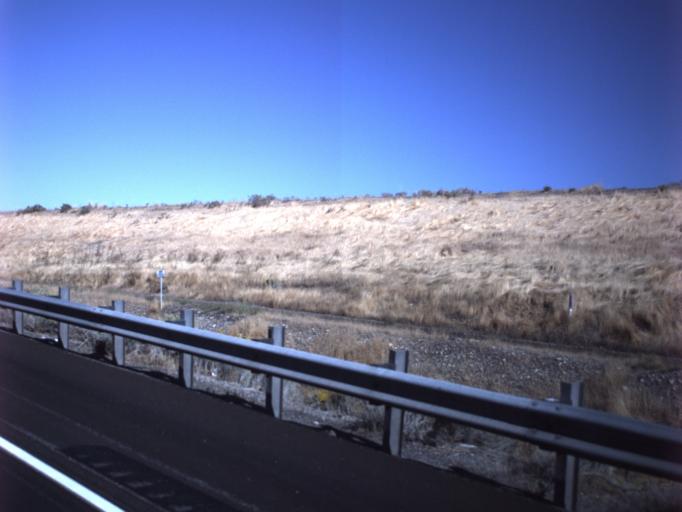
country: US
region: Utah
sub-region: Salt Lake County
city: Magna
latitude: 40.7211
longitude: -112.1517
